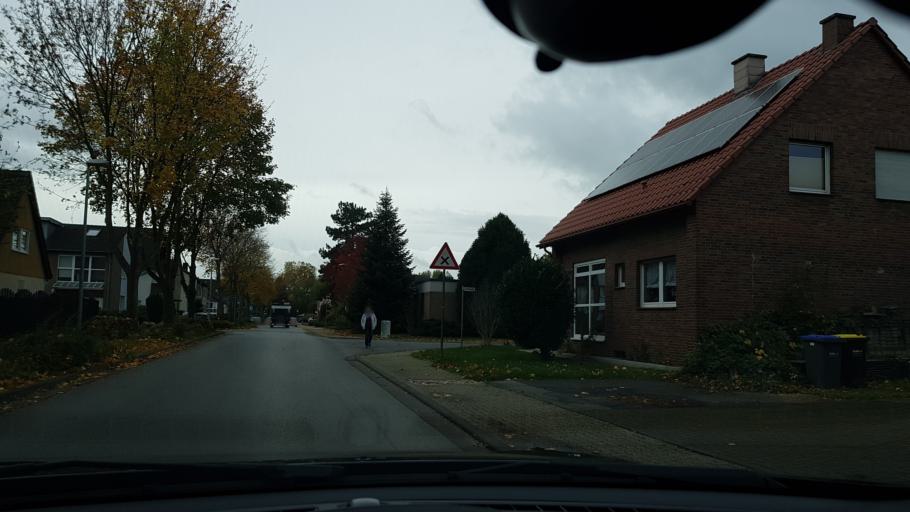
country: DE
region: North Rhine-Westphalia
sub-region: Regierungsbezirk Koln
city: Bedburg
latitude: 51.0009
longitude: 6.5756
